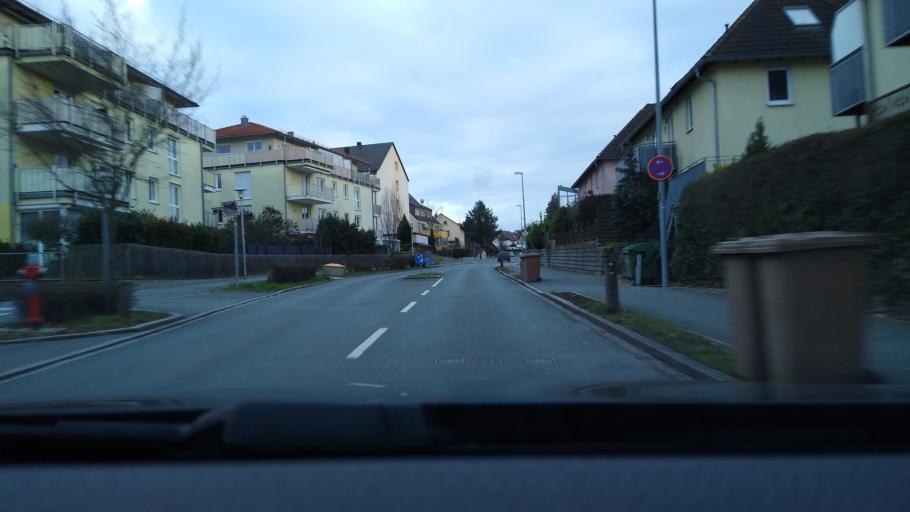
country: DE
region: Bavaria
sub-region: Regierungsbezirk Mittelfranken
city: Oberasbach
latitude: 49.4212
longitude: 10.9823
